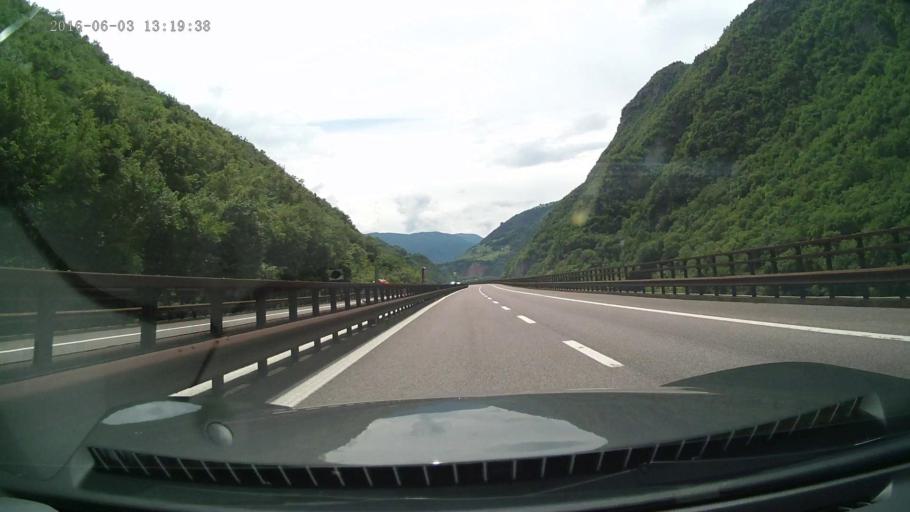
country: IT
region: Trentino-Alto Adige
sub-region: Bolzano
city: Fie Allo Sciliar
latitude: 46.5436
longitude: 11.5067
